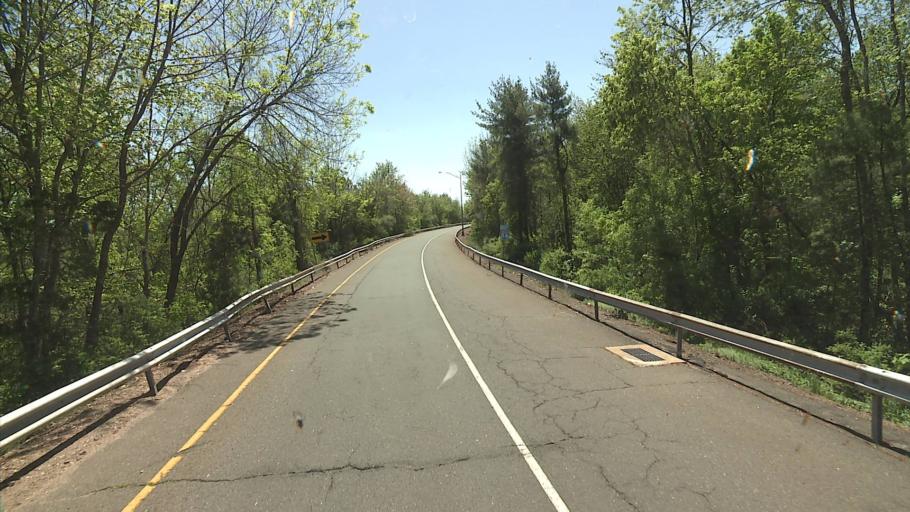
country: US
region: Connecticut
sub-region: Hartford County
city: Farmington
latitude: 41.7227
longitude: -72.7974
